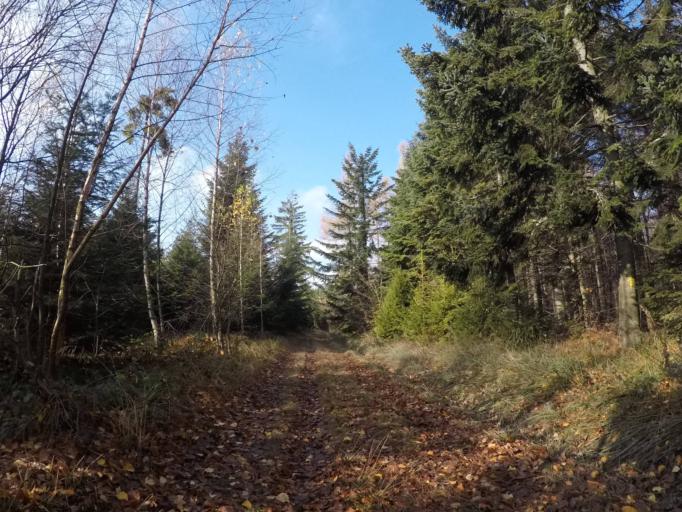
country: SK
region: Kosicky
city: Gelnica
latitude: 48.7643
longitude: 21.0655
